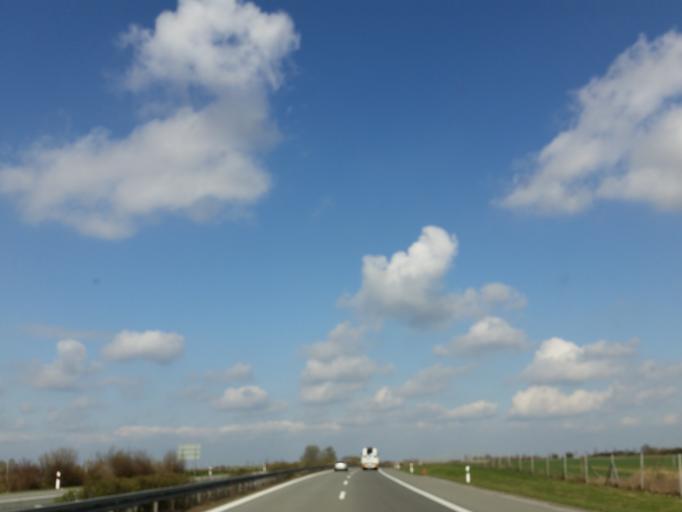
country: DE
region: Mecklenburg-Vorpommern
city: Neuenkirchen
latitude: 53.5972
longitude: 13.3835
